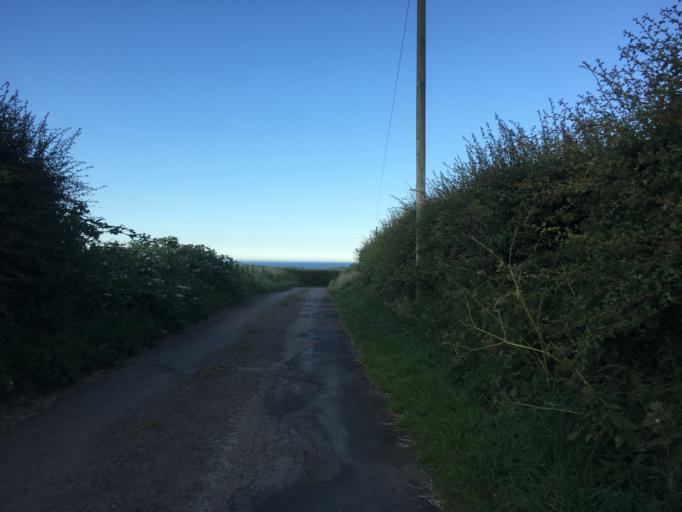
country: GB
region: England
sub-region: Northumberland
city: North Sunderland
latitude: 55.5916
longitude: -1.6879
